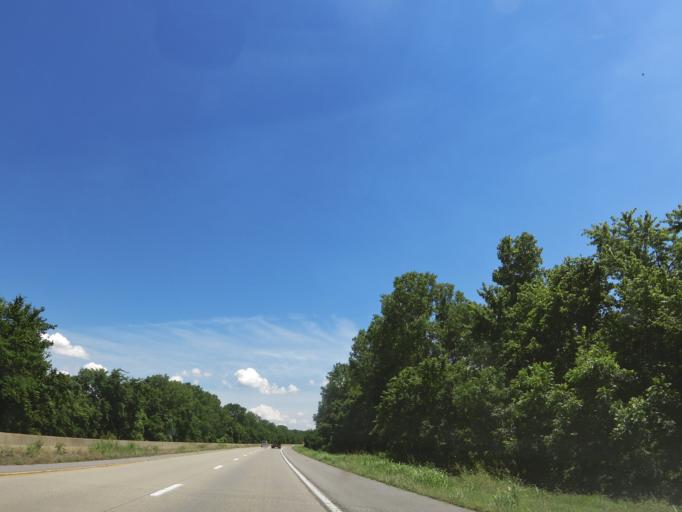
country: US
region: Missouri
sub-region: Pemiscot County
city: Caruthersville
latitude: 36.1289
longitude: -89.6218
